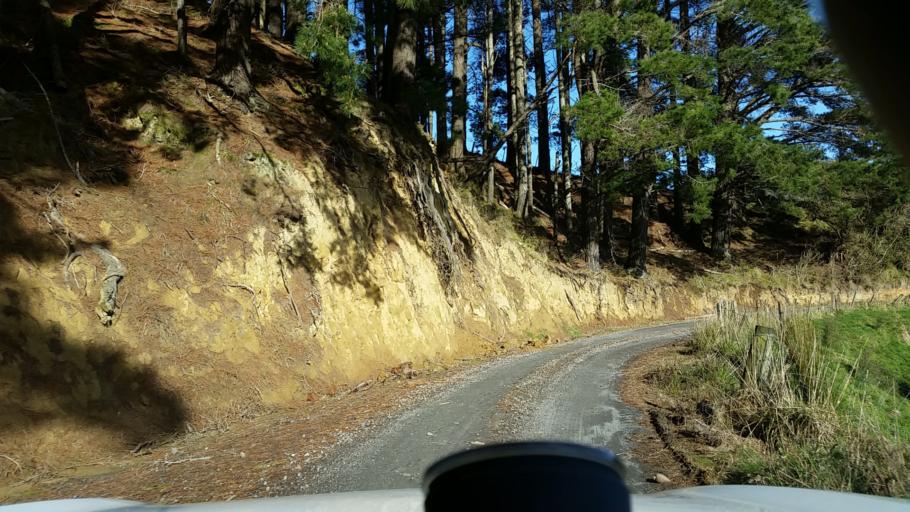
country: NZ
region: Taranaki
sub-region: South Taranaki District
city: Eltham
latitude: -39.4097
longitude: 174.5343
